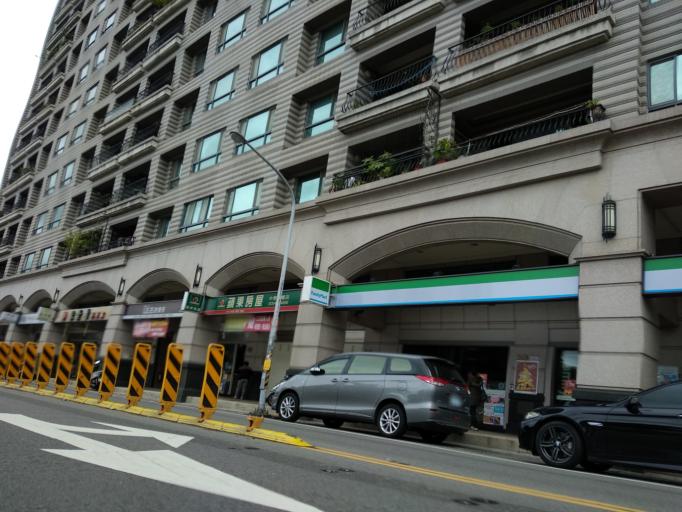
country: TW
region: Taiwan
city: Taoyuan City
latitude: 24.9631
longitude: 121.2174
